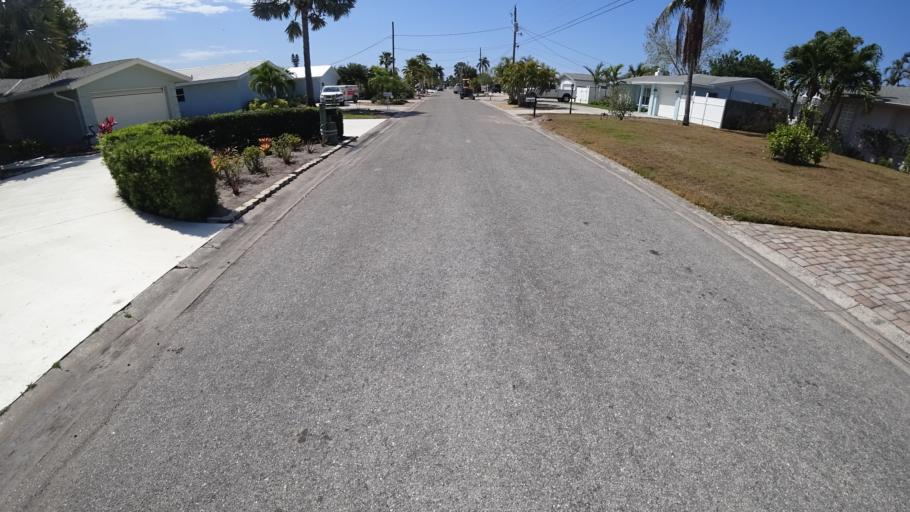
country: US
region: Florida
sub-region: Manatee County
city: Cortez
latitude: 27.4678
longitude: -82.6617
